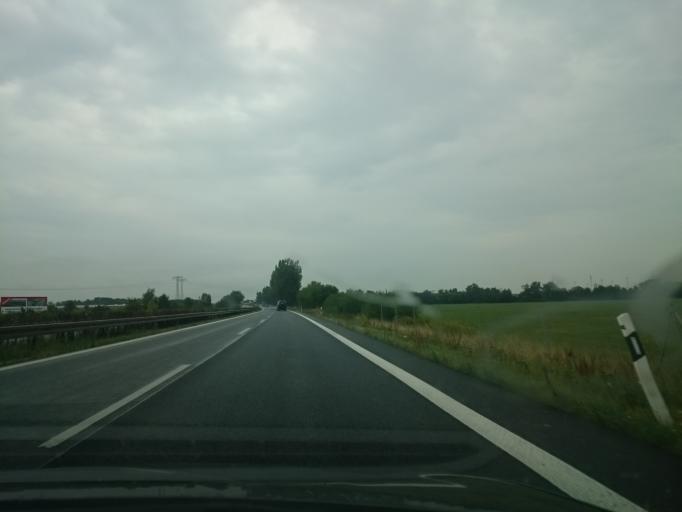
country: DE
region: Brandenburg
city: Brieselang
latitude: 52.6023
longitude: 12.9698
